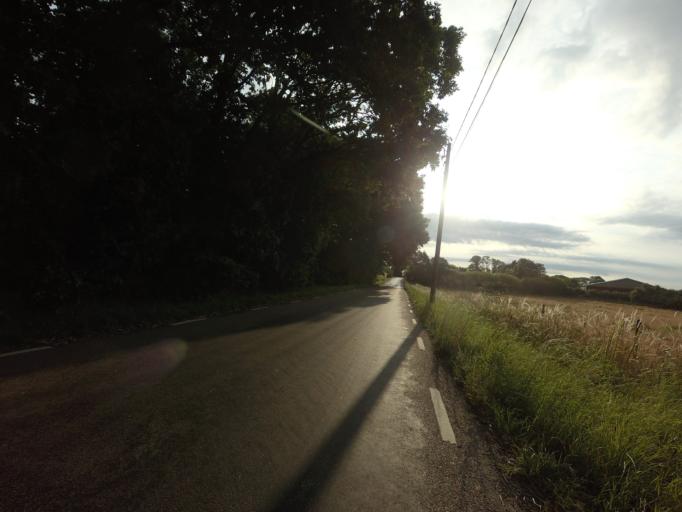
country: SE
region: Skane
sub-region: Helsingborg
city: Odakra
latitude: 56.1564
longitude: 12.7008
